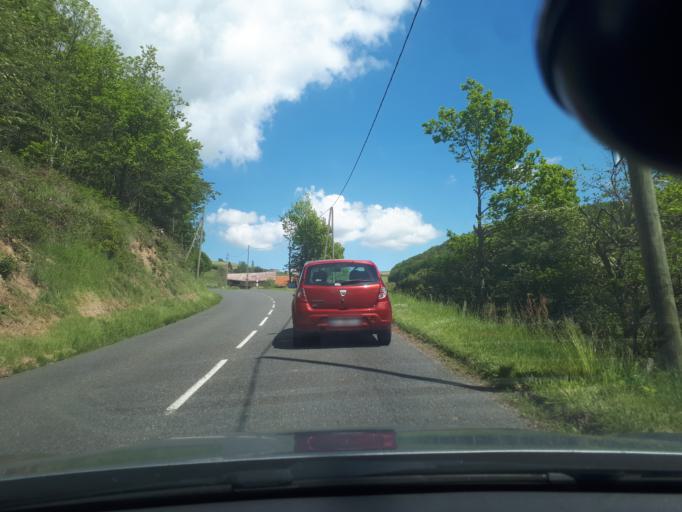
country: FR
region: Rhone-Alpes
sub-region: Departement du Rhone
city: Aveize
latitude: 45.6898
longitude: 4.5086
